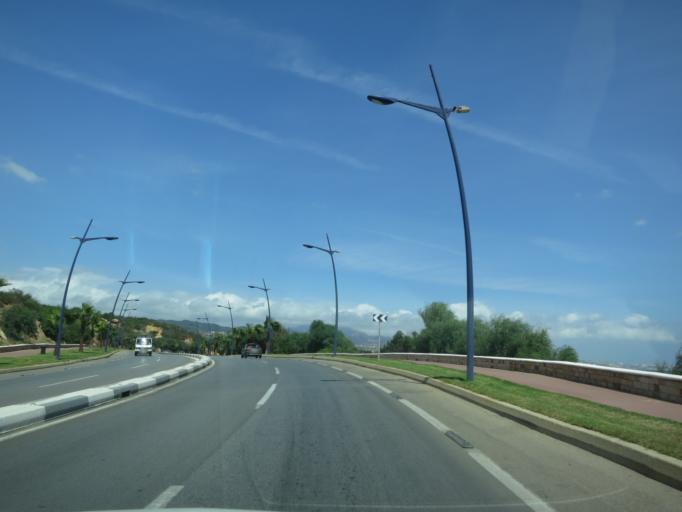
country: ES
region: Ceuta
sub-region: Ceuta
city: Ceuta
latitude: 35.7819
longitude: -5.3495
